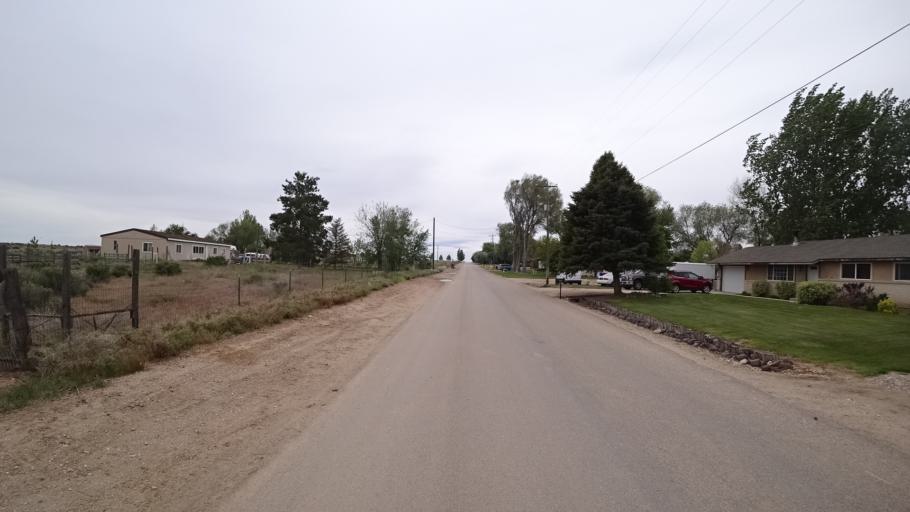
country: US
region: Idaho
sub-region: Ada County
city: Kuna
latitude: 43.4866
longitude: -116.3144
